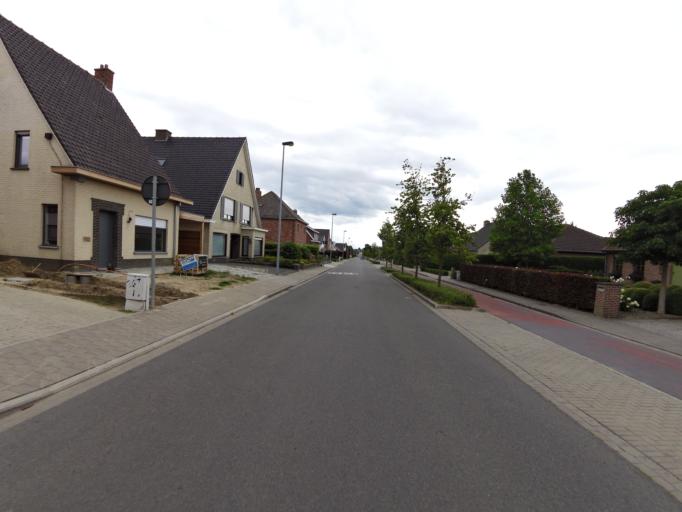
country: BE
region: Flanders
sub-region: Provincie West-Vlaanderen
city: Kortemark
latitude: 50.9998
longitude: 3.0357
